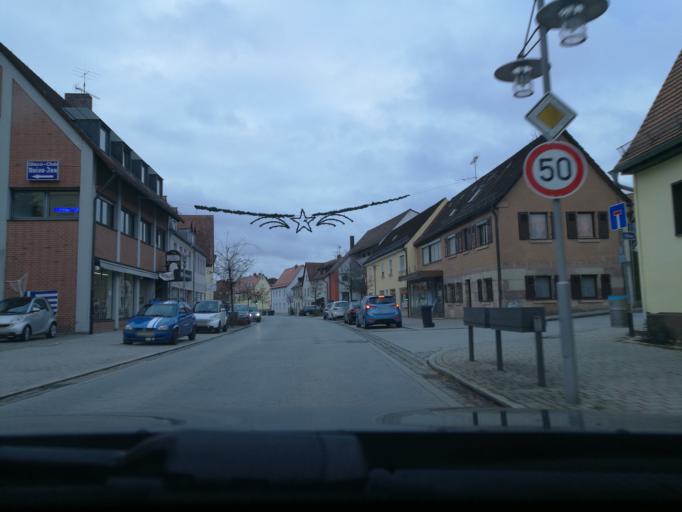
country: DE
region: Bavaria
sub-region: Regierungsbezirk Mittelfranken
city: Heroldsberg
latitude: 49.5314
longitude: 11.1514
